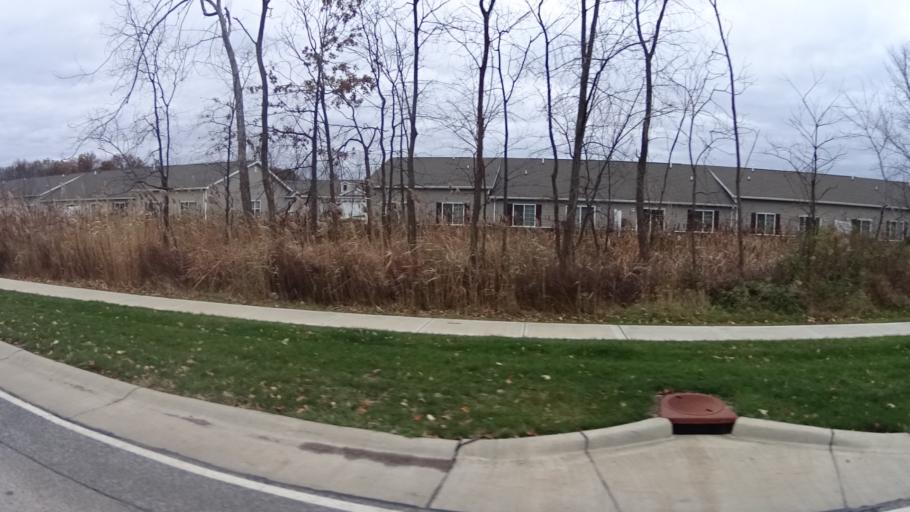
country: US
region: Ohio
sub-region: Lorain County
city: Avon Lake
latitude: 41.4887
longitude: -82.0291
